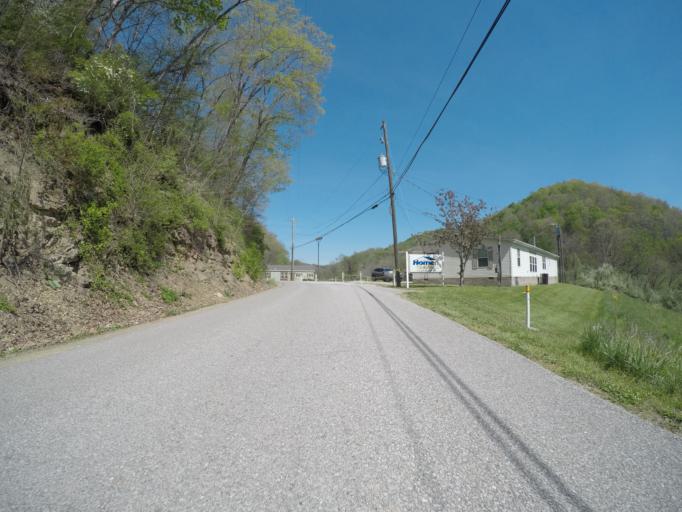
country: US
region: West Virginia
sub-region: Kanawha County
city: Charleston
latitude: 38.4129
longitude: -81.6261
